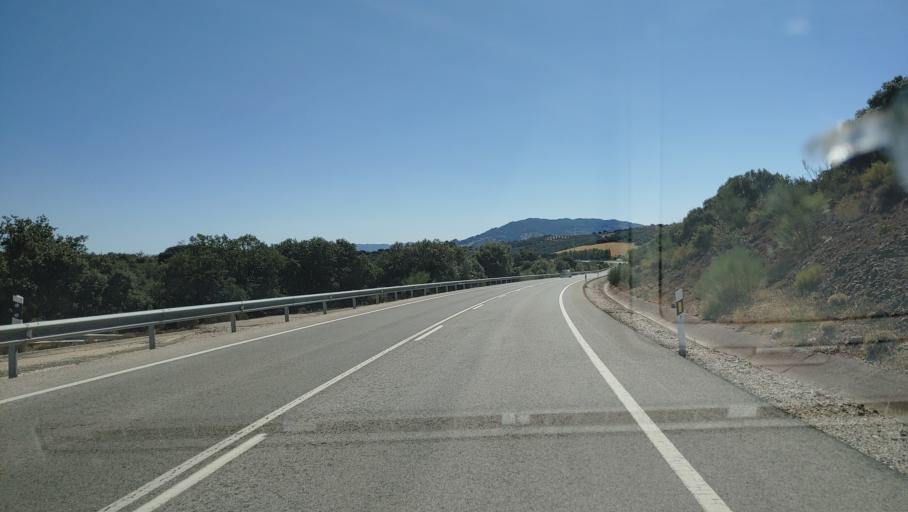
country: ES
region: Andalusia
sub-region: Provincia de Jaen
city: Genave
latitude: 38.4634
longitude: -2.7622
